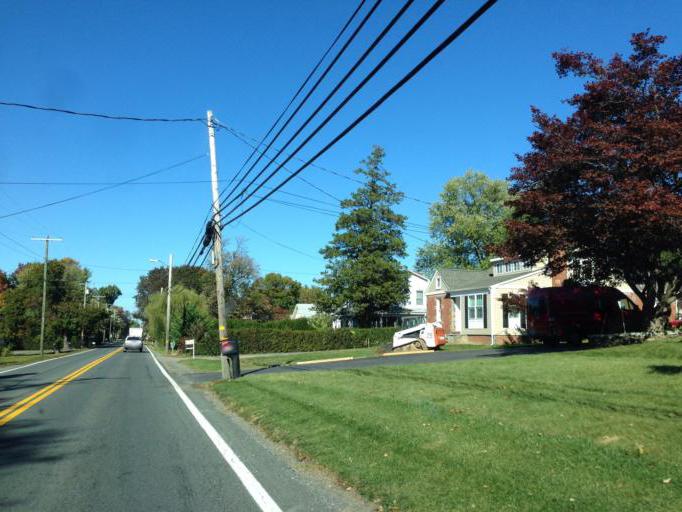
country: US
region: Maryland
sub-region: Montgomery County
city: Damascus
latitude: 39.2928
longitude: -77.2048
